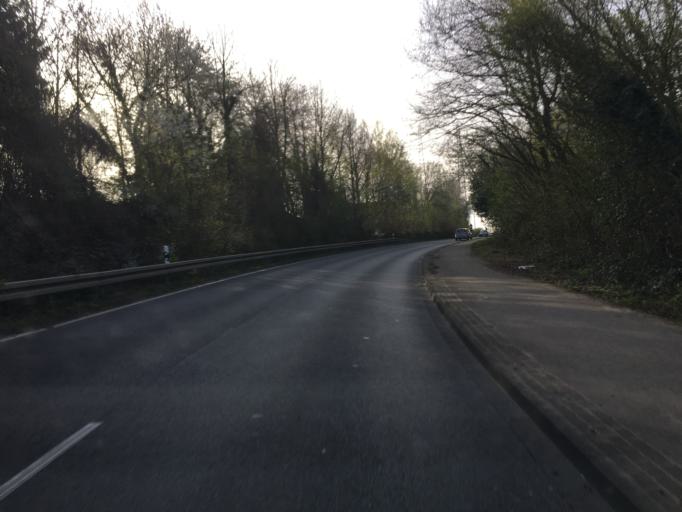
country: DE
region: North Rhine-Westphalia
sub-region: Regierungsbezirk Koln
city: Hurth
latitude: 50.8631
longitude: 6.8571
